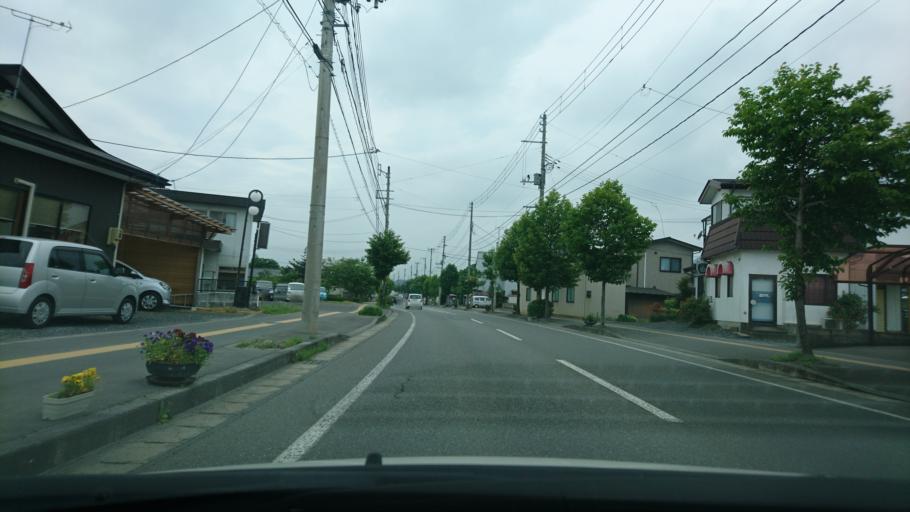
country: JP
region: Iwate
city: Ichinoseki
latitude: 38.9335
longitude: 141.1107
